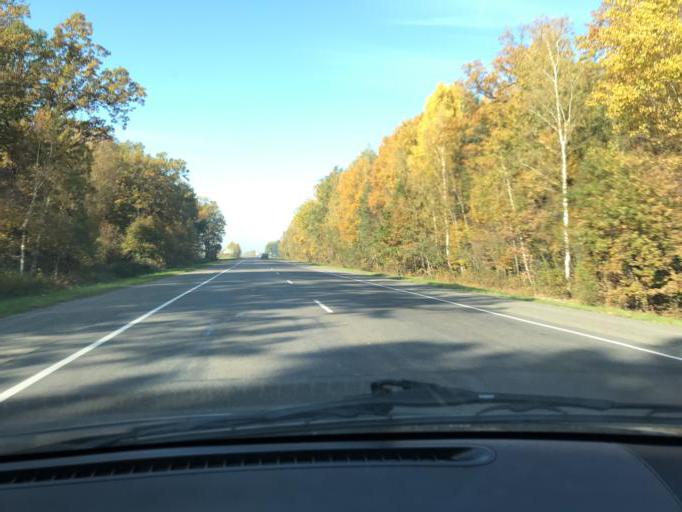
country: BY
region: Brest
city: Horad Luninyets
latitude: 52.3090
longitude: 26.6781
